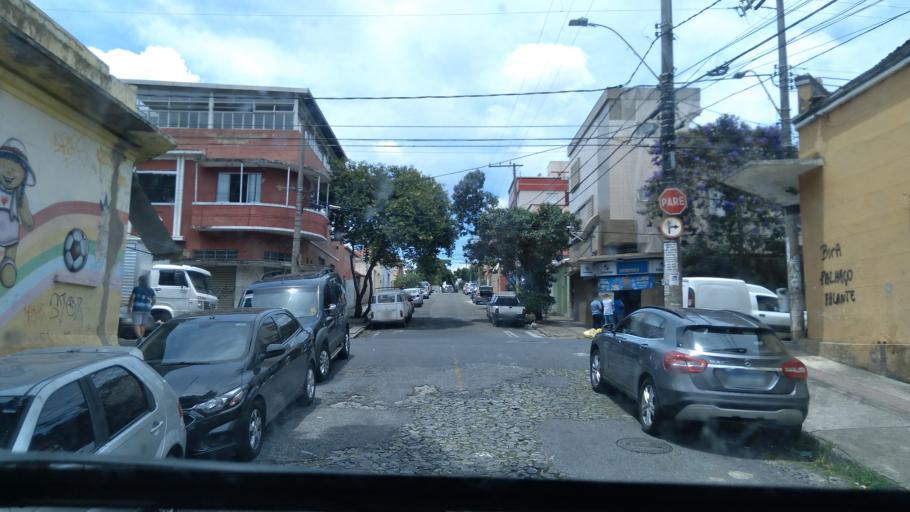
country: BR
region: Minas Gerais
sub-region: Belo Horizonte
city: Belo Horizonte
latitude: -19.9171
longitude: -43.9159
